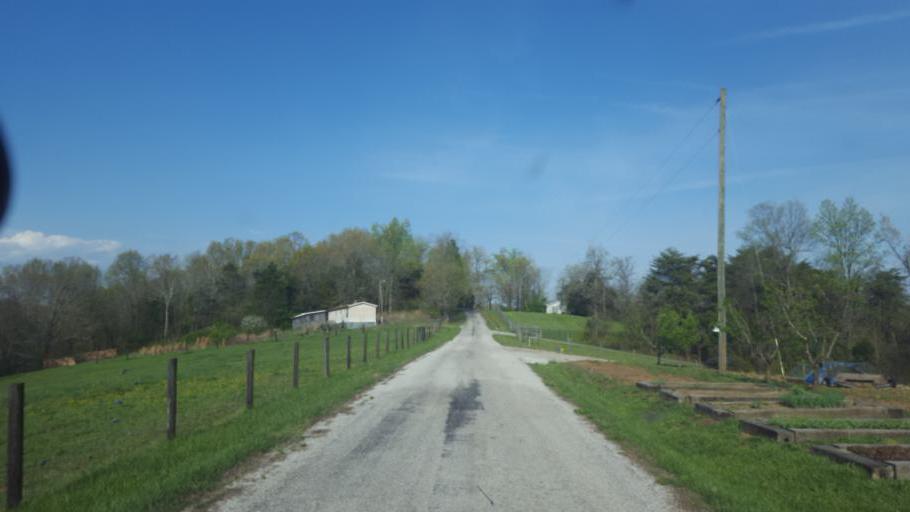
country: US
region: Kentucky
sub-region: Edmonson County
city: Brownsville
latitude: 37.3277
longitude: -86.1026
